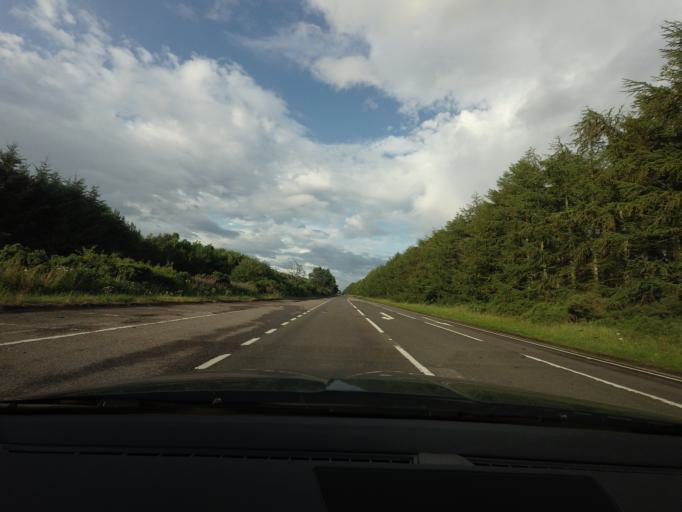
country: GB
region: Scotland
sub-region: Highland
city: Nairn
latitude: 57.5654
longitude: -3.9488
